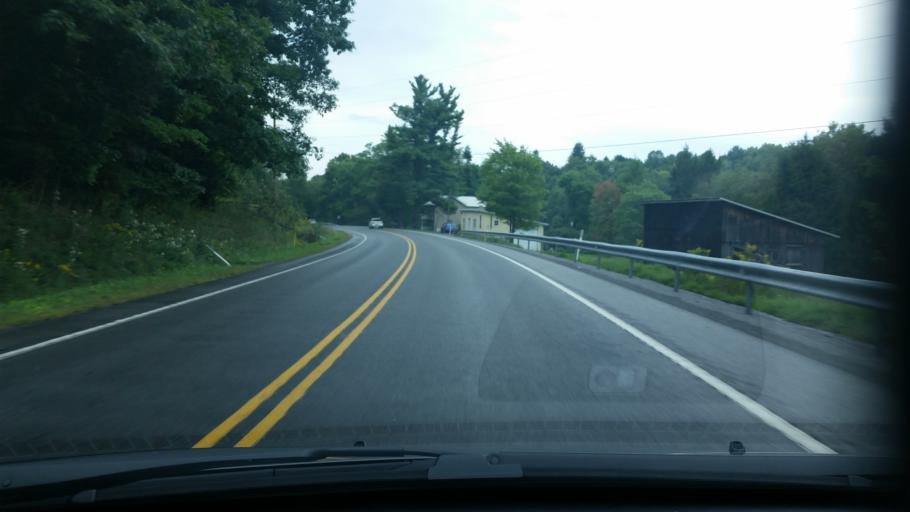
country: US
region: Pennsylvania
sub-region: Clearfield County
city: Shiloh
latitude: 41.1004
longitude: -78.2448
